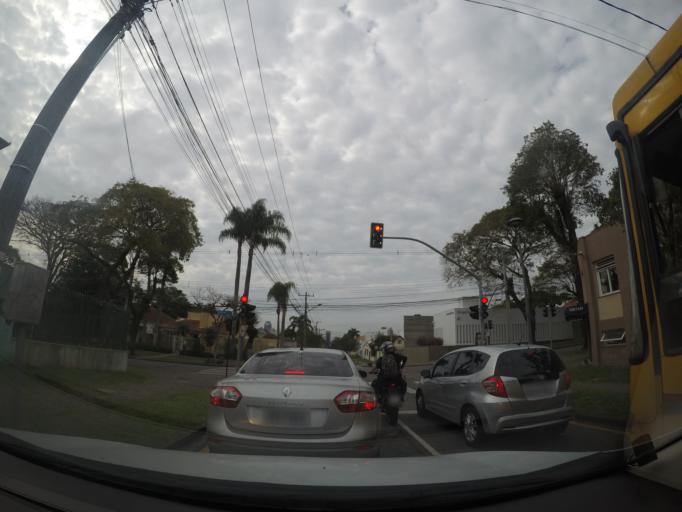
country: BR
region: Parana
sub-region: Curitiba
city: Curitiba
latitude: -25.4170
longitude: -49.2769
